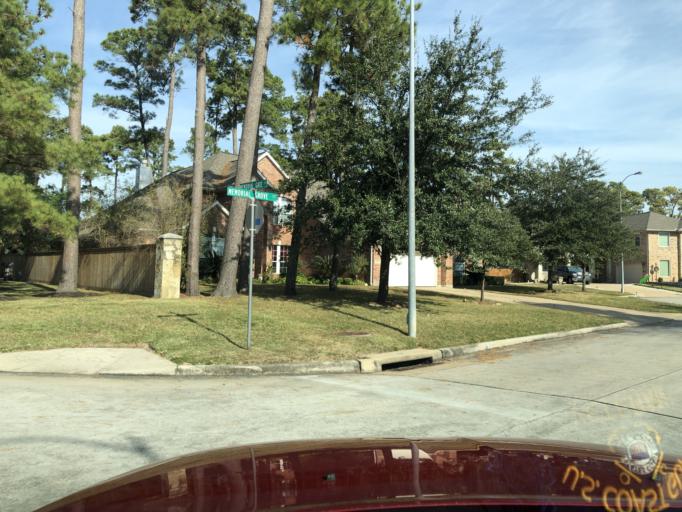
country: US
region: Texas
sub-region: Harris County
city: Tomball
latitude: 30.0277
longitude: -95.5595
